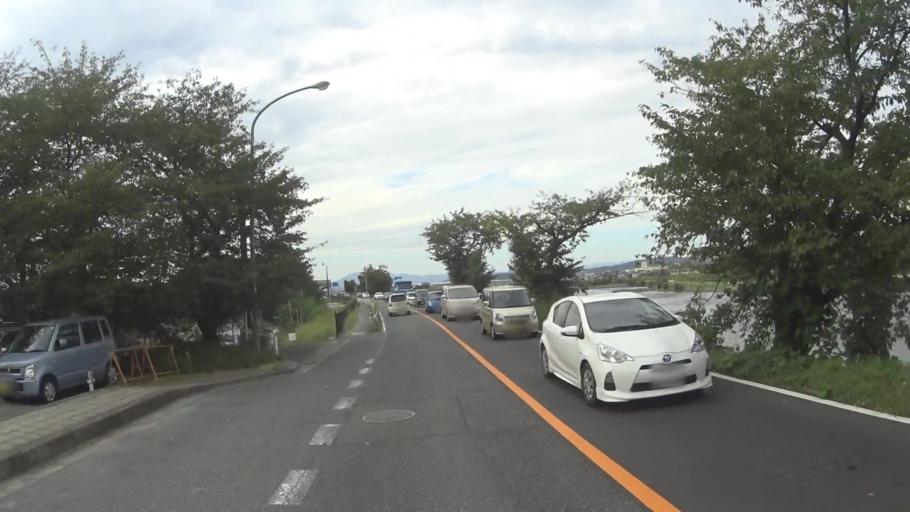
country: JP
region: Kyoto
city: Uji
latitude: 34.8933
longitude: 135.8047
